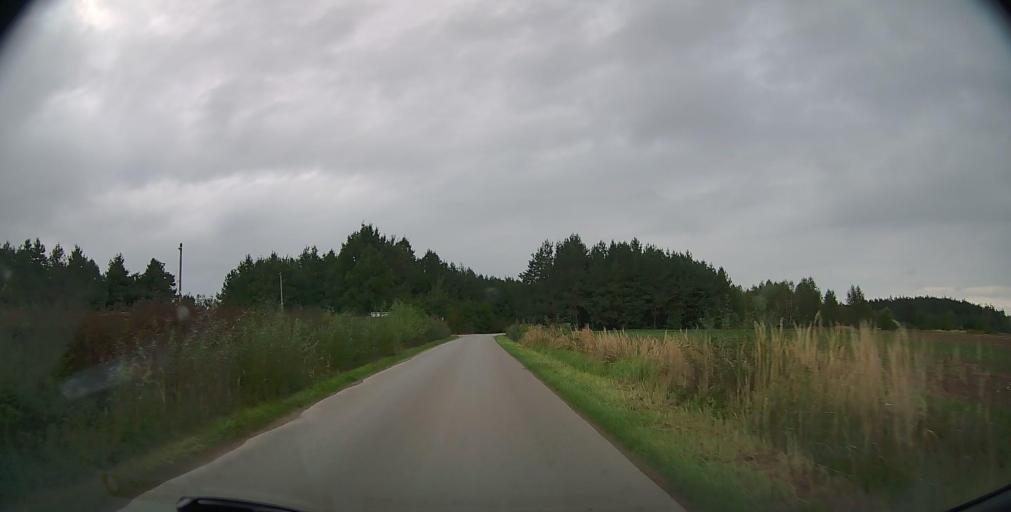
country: PL
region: Masovian Voivodeship
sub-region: Powiat radomski
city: Jedlinsk
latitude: 51.4583
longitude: 21.1040
